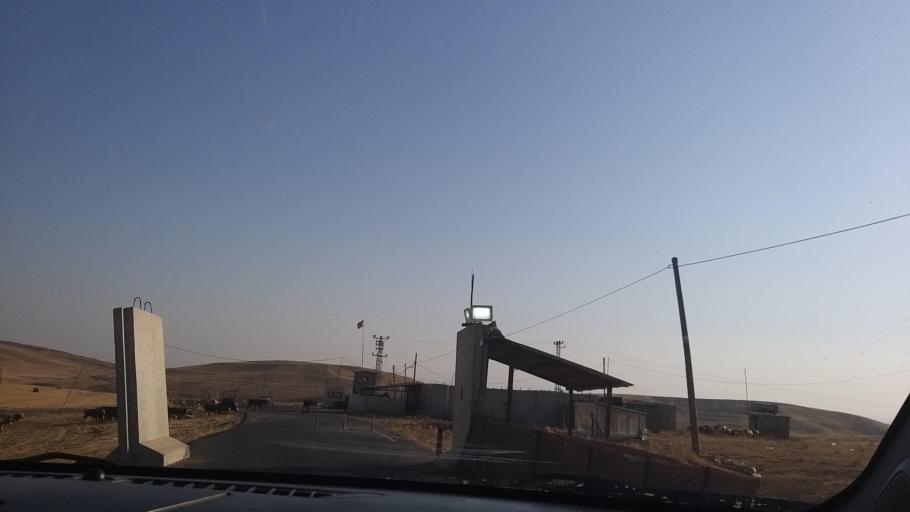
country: TR
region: Diyarbakir
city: Silvan
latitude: 38.1858
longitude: 41.0065
